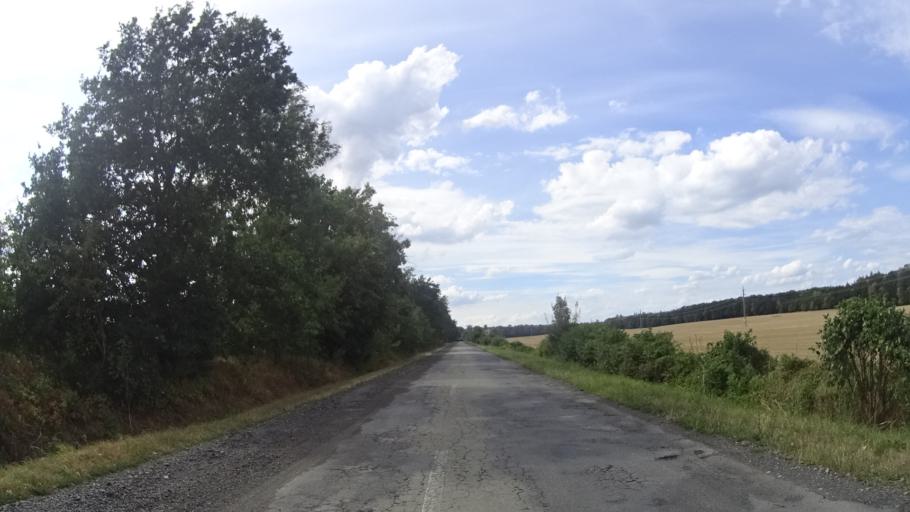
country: CZ
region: Olomoucky
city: Cervenka
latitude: 49.7167
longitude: 17.0461
